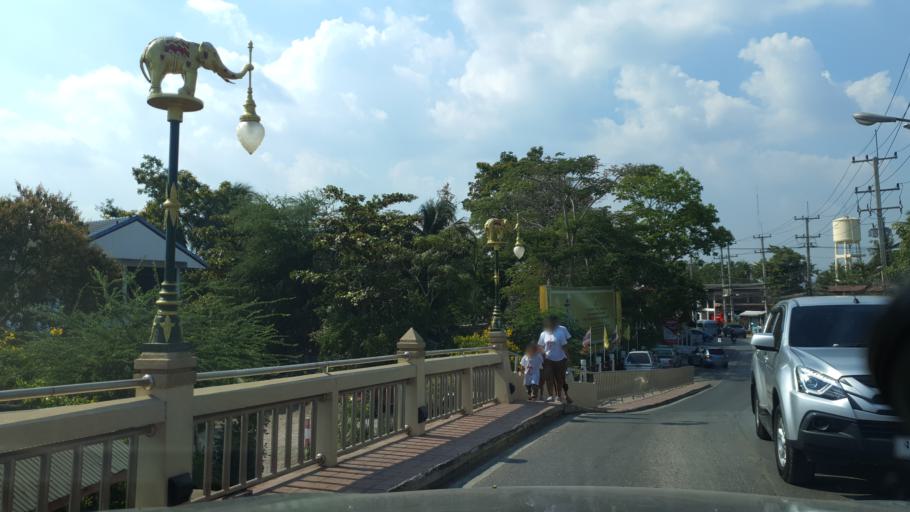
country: TH
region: Samut Songkhram
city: Amphawa
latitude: 13.4260
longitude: 99.9551
